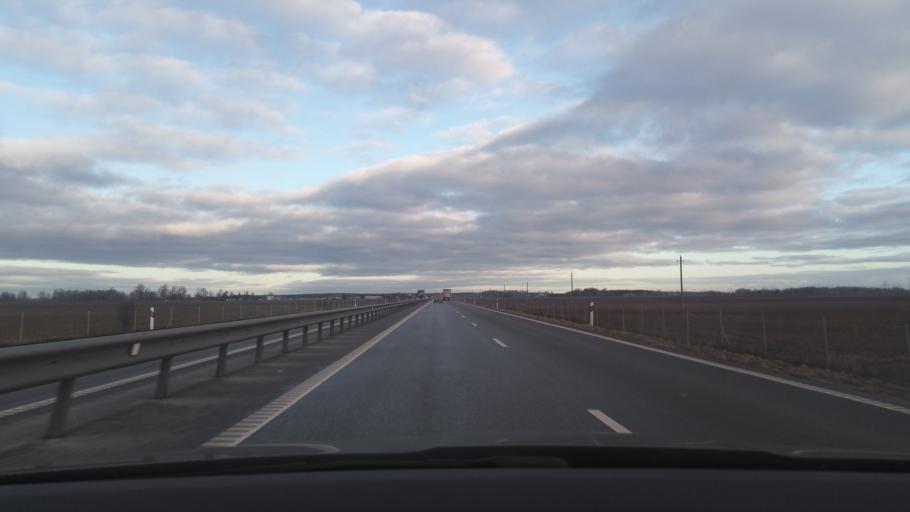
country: LT
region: Panevezys
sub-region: Panevezys City
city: Panevezys
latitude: 55.7019
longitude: 24.2727
